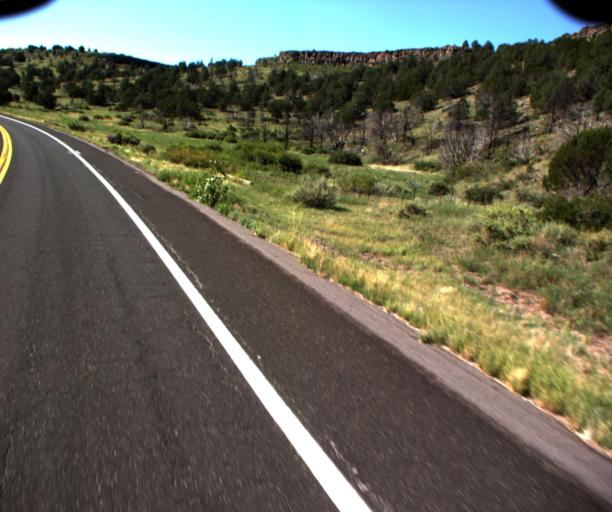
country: US
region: Arizona
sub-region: Apache County
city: Eagar
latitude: 34.0844
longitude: -109.2029
